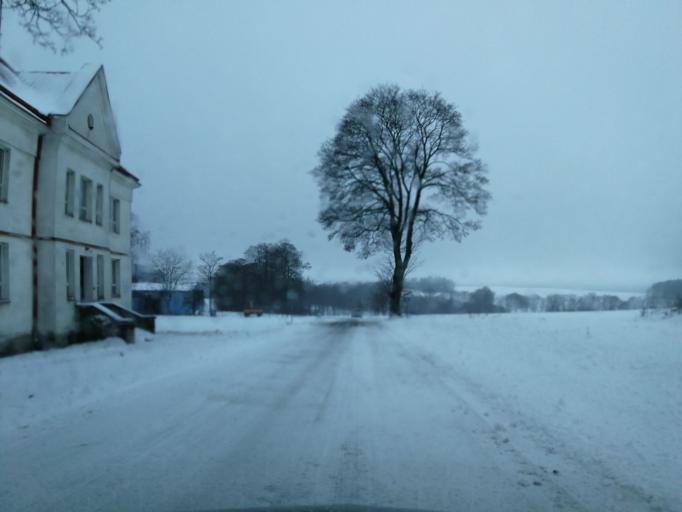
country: CZ
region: Vysocina
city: Heralec
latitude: 49.5325
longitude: 15.4506
